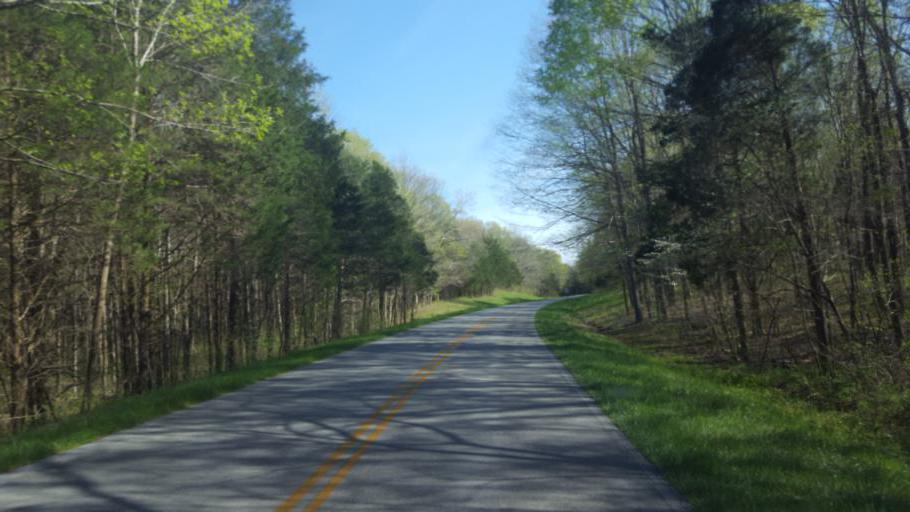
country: US
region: Kentucky
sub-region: Edmonson County
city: Brownsville
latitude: 37.1559
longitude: -86.1242
